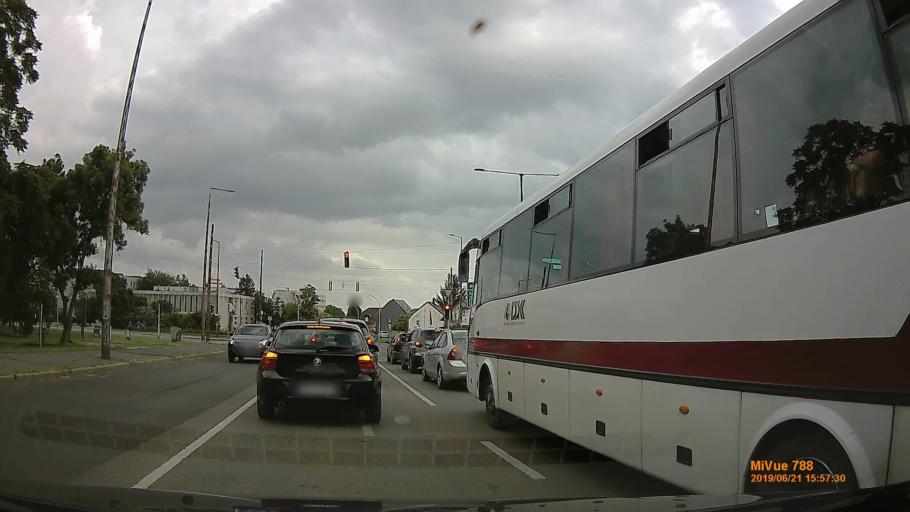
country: HU
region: Baranya
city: Pellerd
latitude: 46.0656
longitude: 18.1892
